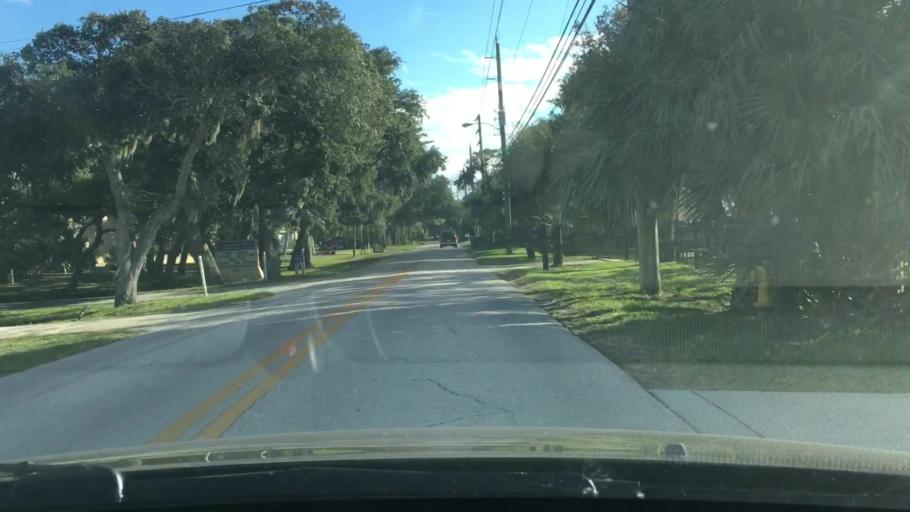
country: US
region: Florida
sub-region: Volusia County
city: Ormond-by-the-Sea
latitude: 29.3472
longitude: -81.0731
